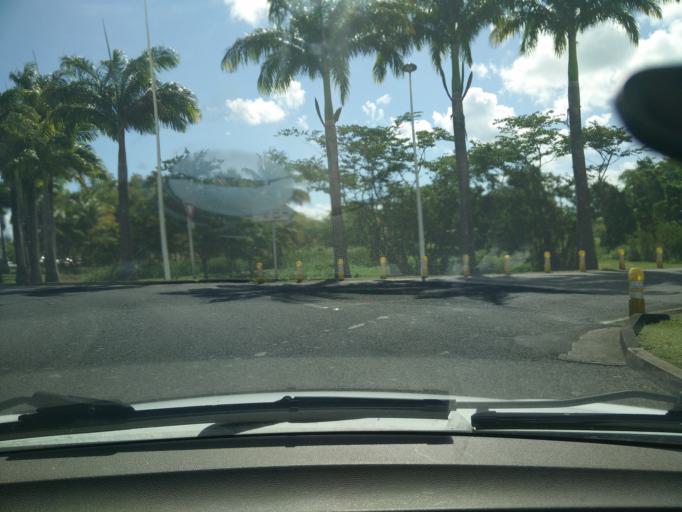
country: GP
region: Guadeloupe
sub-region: Guadeloupe
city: Les Abymes
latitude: 16.2738
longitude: -61.5244
